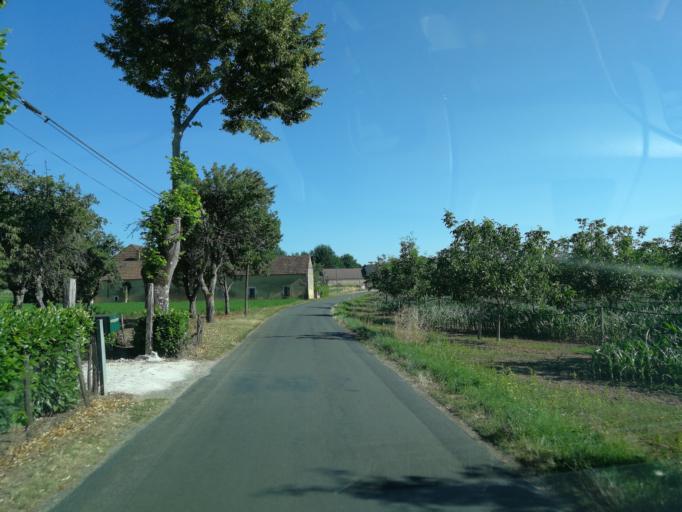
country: FR
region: Midi-Pyrenees
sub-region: Departement du Lot
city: Gourdon
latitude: 44.8287
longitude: 1.3606
